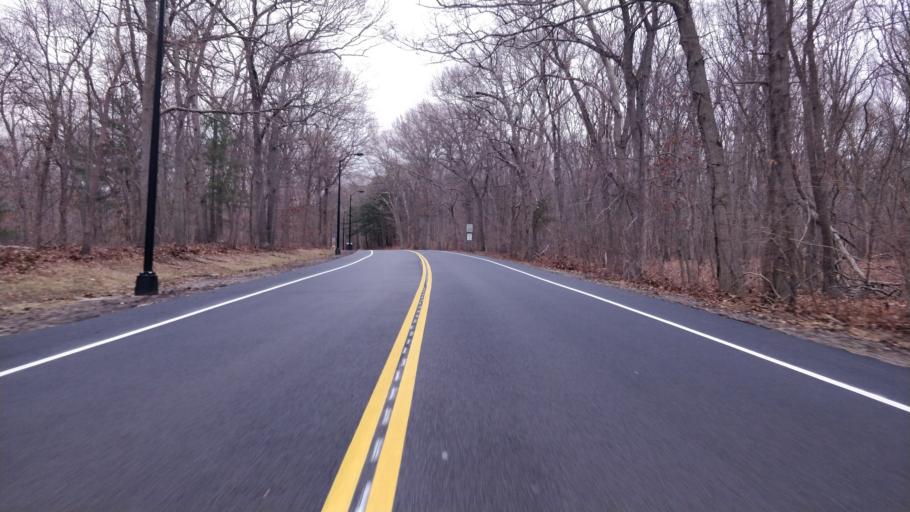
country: US
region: New York
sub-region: Nassau County
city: Brookville
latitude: 40.7928
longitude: -73.5640
